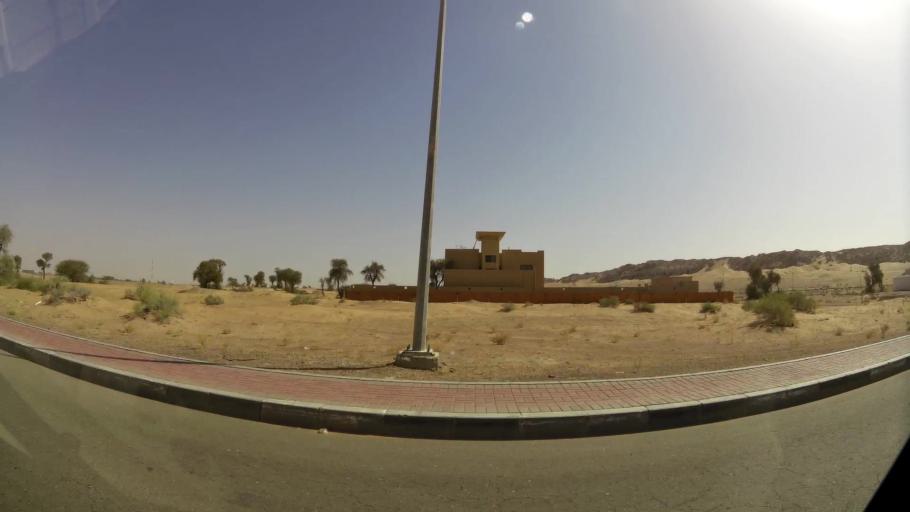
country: OM
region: Al Buraimi
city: Al Buraymi
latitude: 24.3218
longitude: 55.8103
